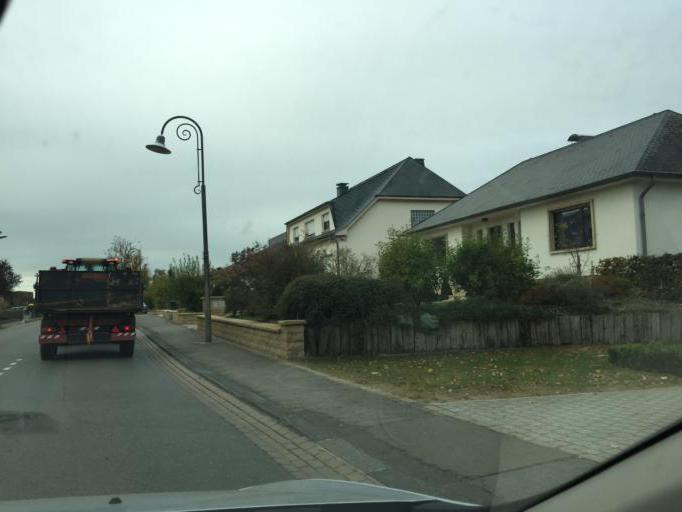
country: LU
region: Luxembourg
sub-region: Canton de Capellen
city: Kopstal
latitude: 49.6853
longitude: 6.0579
